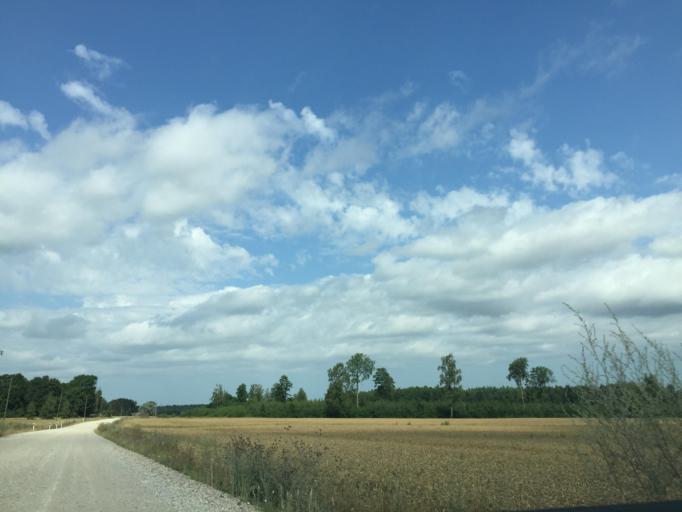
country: LV
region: Kandava
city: Kandava
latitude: 56.9939
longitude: 22.8936
